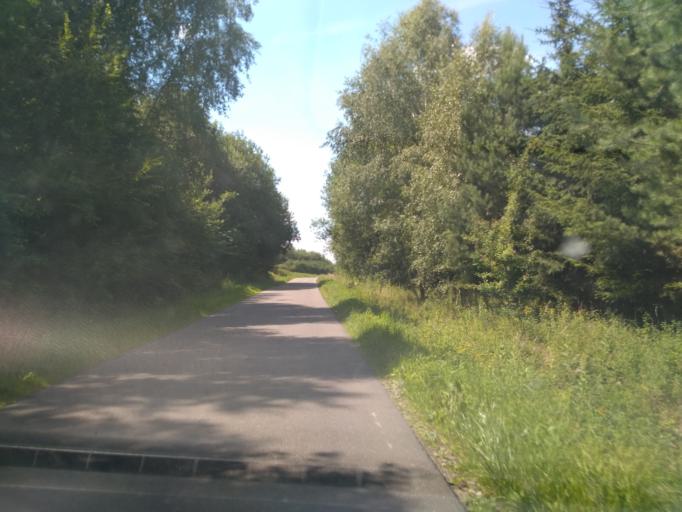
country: PL
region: Subcarpathian Voivodeship
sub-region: Powiat strzyzowski
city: Jawornik
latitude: 49.8592
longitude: 21.8809
